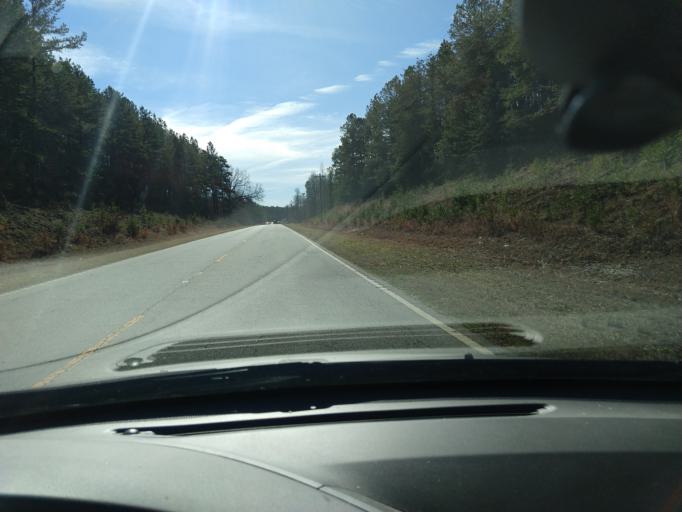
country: US
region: South Carolina
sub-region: Oconee County
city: Westminster
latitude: 34.6305
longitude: -83.1359
